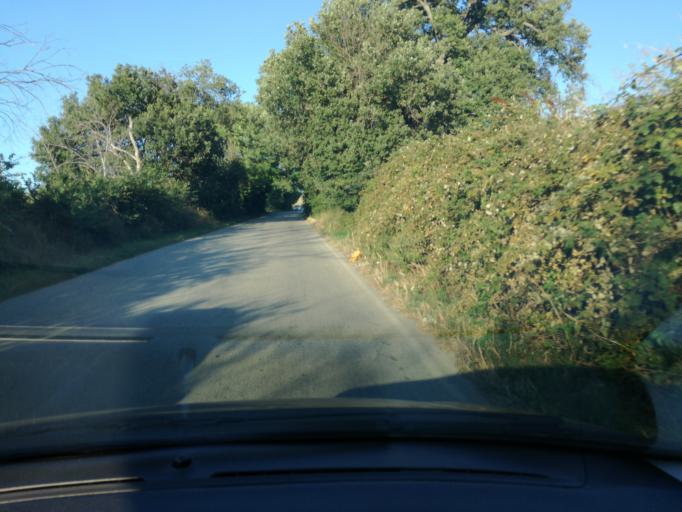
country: IT
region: Molise
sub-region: Provincia di Campobasso
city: San Giacomo degli Schiavoni
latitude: 41.9346
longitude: 14.9437
